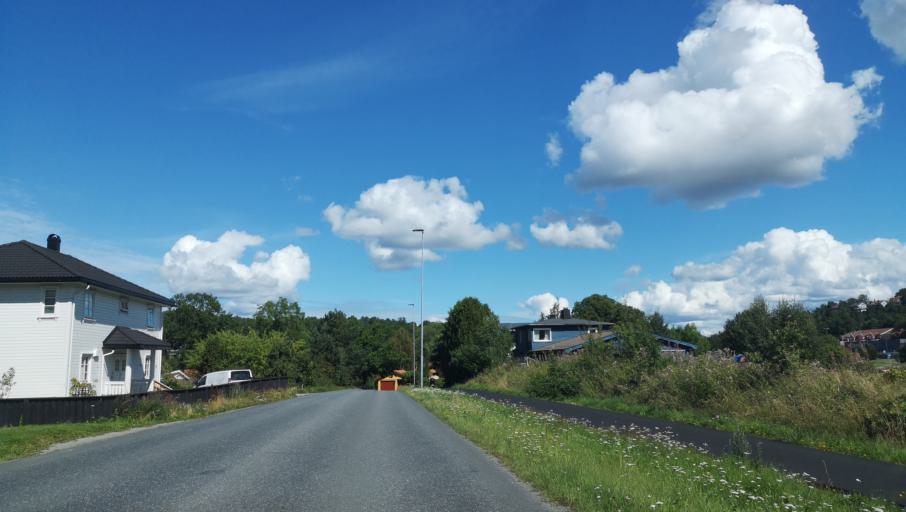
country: NO
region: Akershus
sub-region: Frogn
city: Drobak
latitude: 59.6652
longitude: 10.6408
